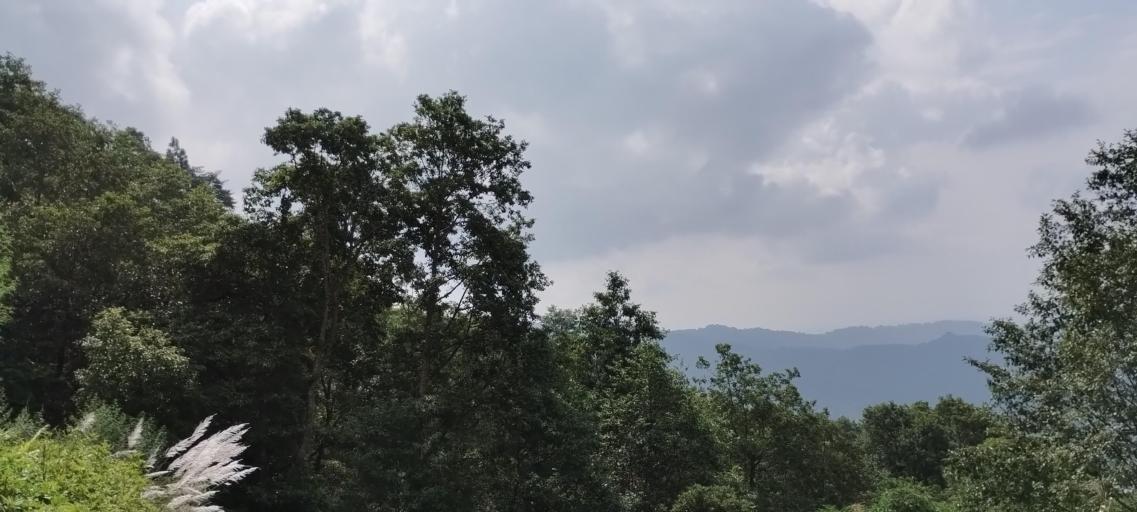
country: NP
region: Central Region
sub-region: Bagmati Zone
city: Kathmandu
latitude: 27.7912
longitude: 85.3594
